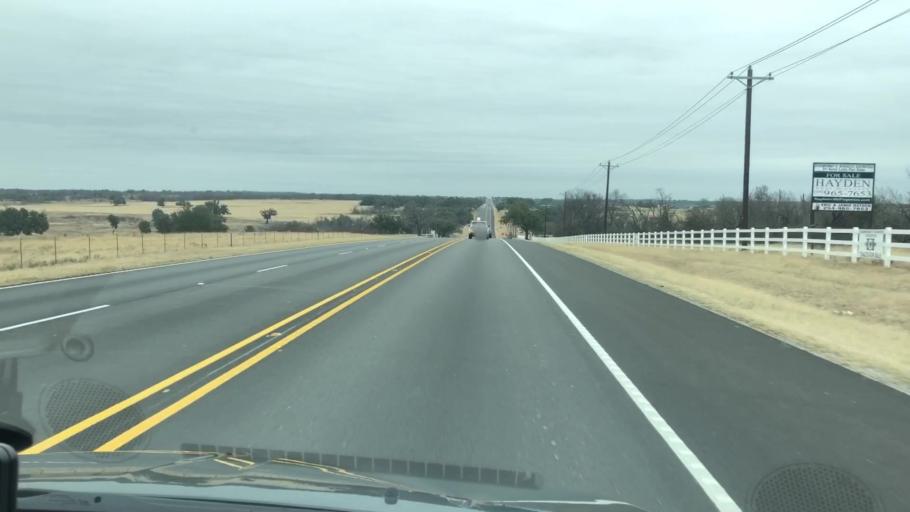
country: US
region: Texas
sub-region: Erath County
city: Stephenville
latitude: 32.2982
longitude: -98.1884
